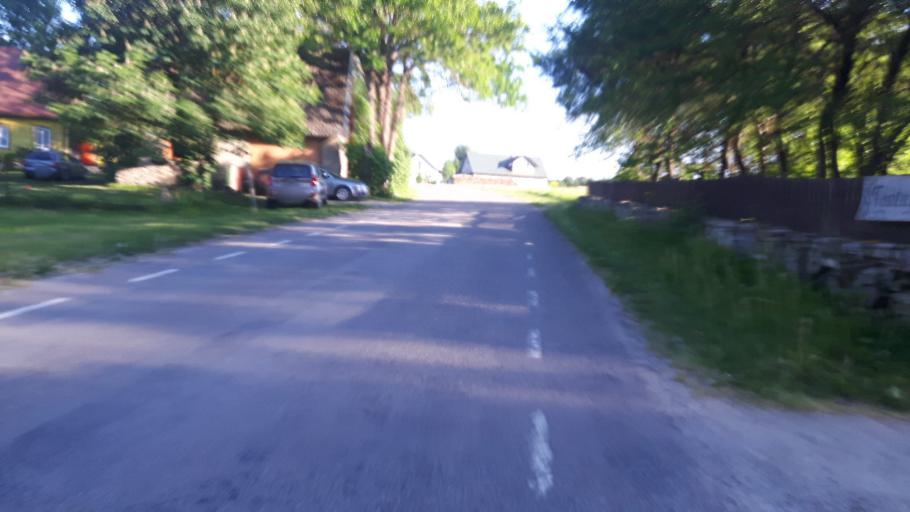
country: EE
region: Raplamaa
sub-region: Kehtna vald
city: Kehtna
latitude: 58.9002
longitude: 24.8786
